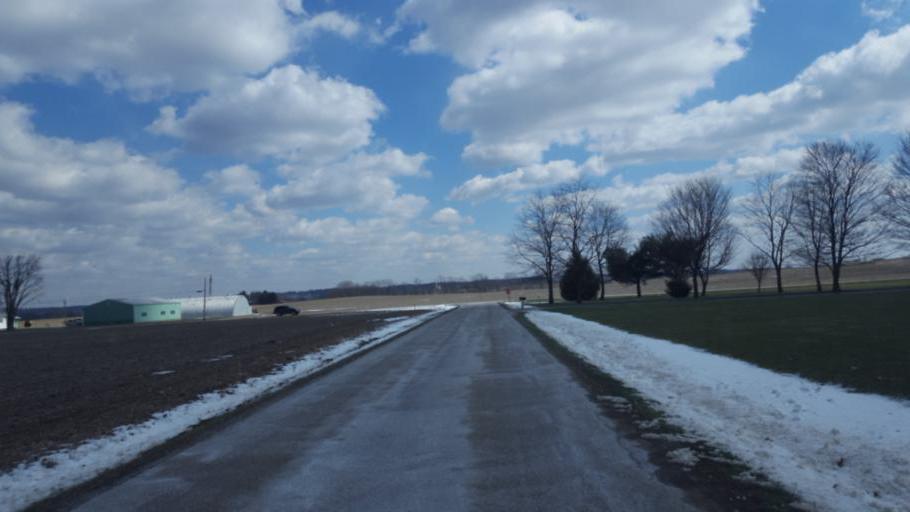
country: US
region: Ohio
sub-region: Knox County
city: Mount Vernon
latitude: 40.3539
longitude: -82.5139
